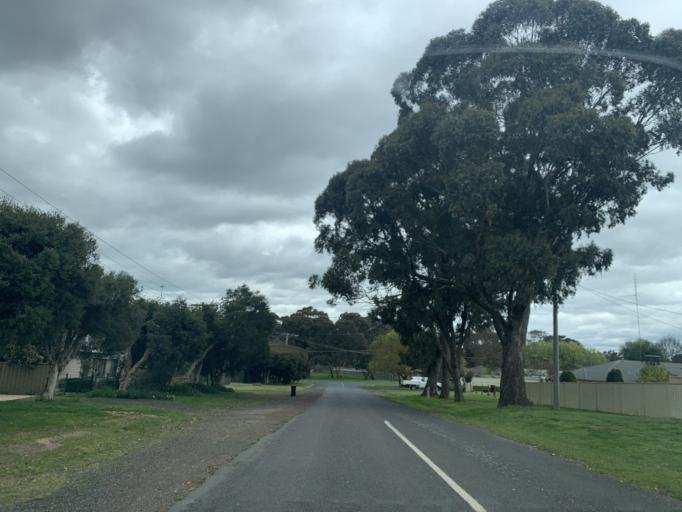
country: AU
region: Victoria
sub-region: Whittlesea
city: Whittlesea
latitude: -37.2099
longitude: 145.0428
